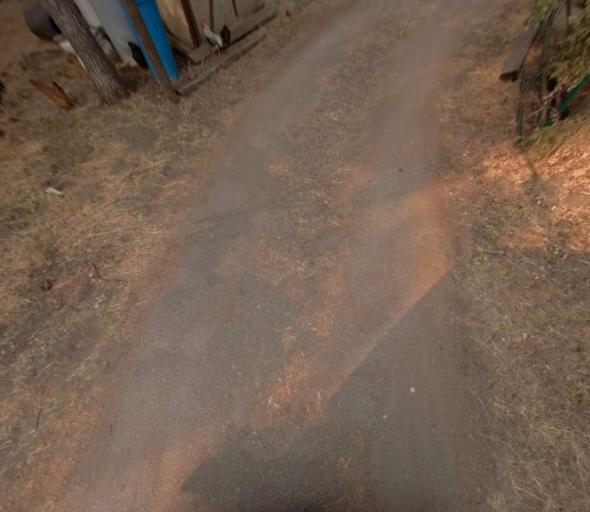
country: US
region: California
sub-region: Madera County
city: Oakhurst
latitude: 37.3230
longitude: -119.6420
